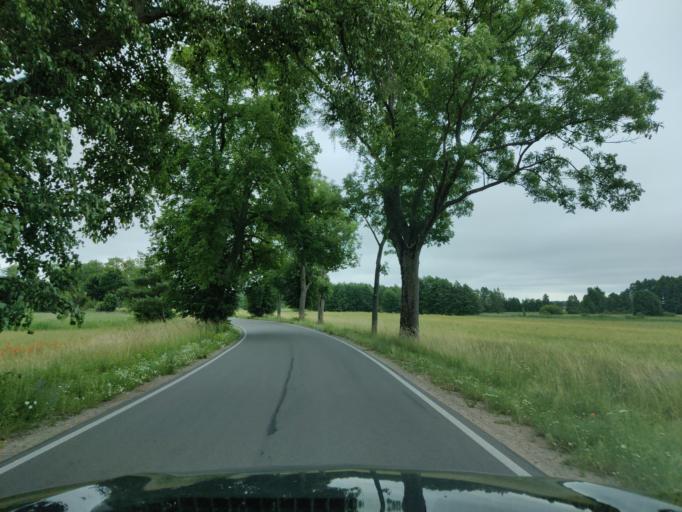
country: PL
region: Warmian-Masurian Voivodeship
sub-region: Powiat gizycki
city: Ryn
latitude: 53.8783
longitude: 21.5839
